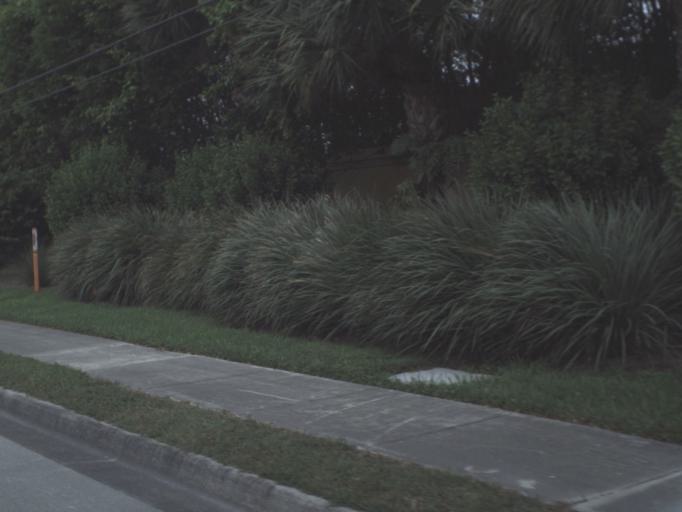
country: US
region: Florida
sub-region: Collier County
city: Lely Resort
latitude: 26.0919
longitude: -81.6874
